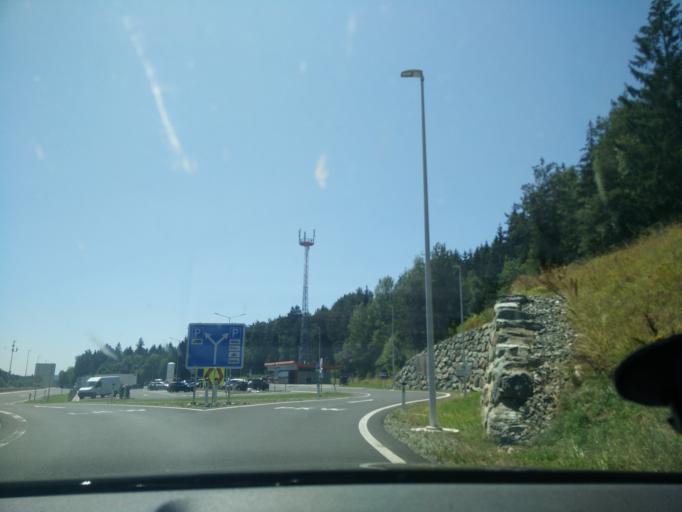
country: AT
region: Styria
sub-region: Politischer Bezirk Hartberg-Fuerstenfeld
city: Hainersdorf
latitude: 47.1200
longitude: 15.9837
